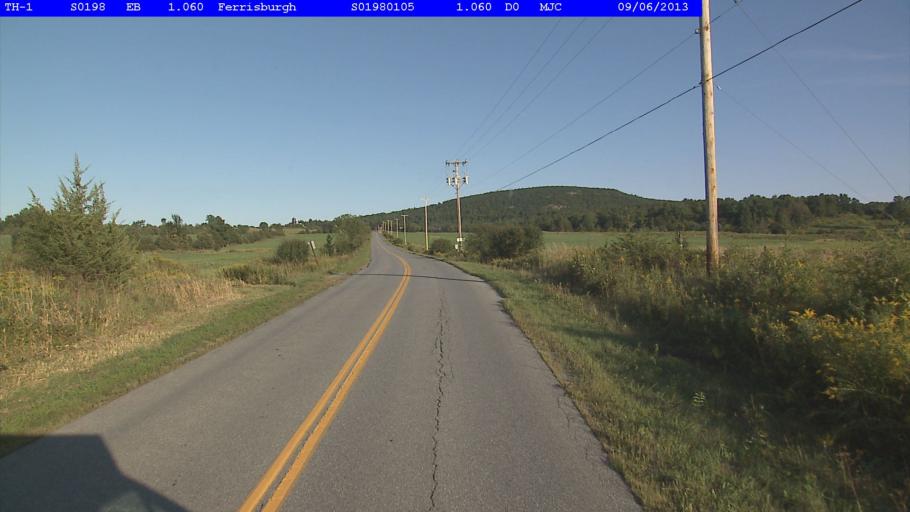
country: US
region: Vermont
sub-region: Addison County
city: Vergennes
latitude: 44.2581
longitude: -73.2075
